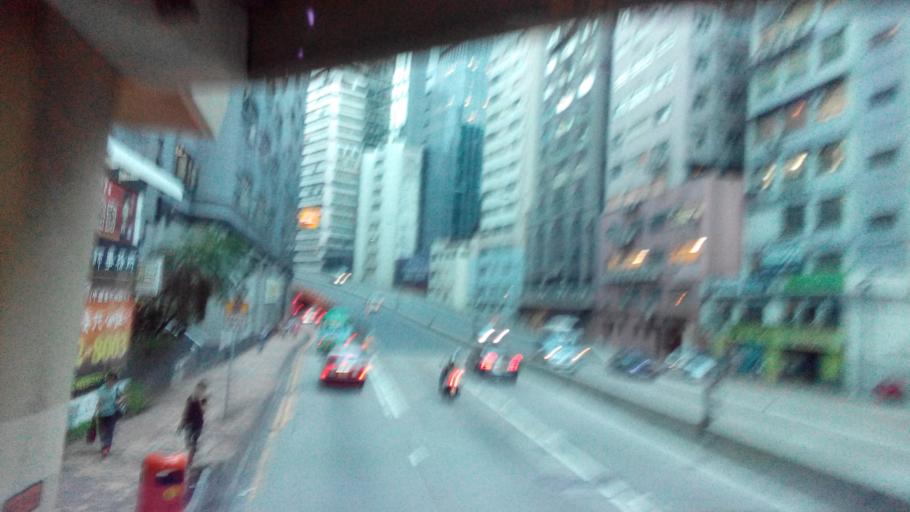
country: HK
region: Wanchai
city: Wan Chai
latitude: 22.2484
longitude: 114.1640
